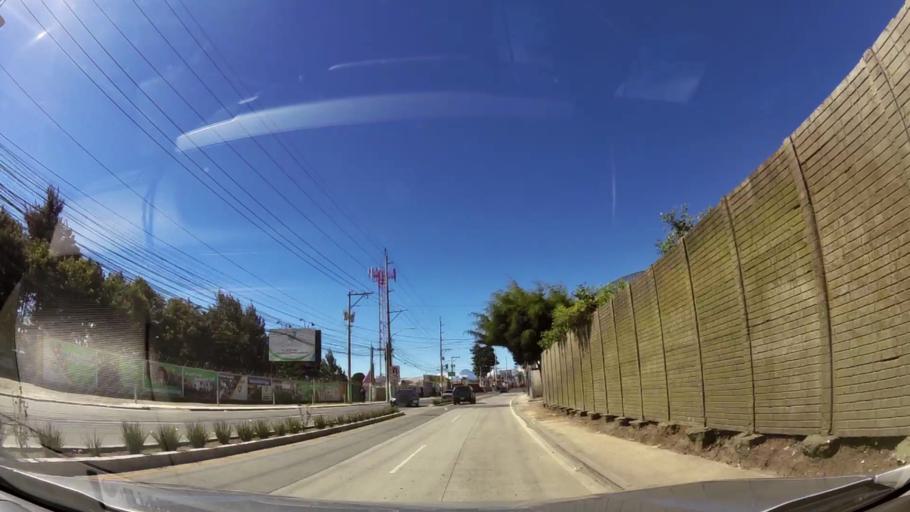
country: GT
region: Guatemala
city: San Jose Pinula
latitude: 14.5436
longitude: -90.4334
